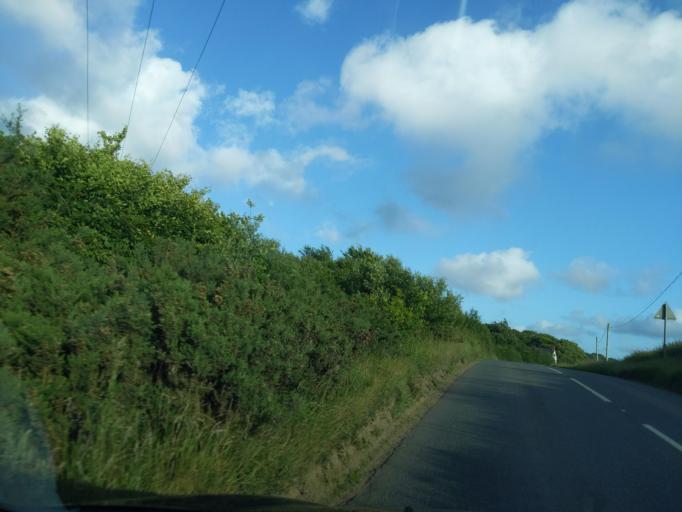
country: GB
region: England
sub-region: Devon
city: Great Torrington
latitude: 50.9918
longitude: -4.0945
